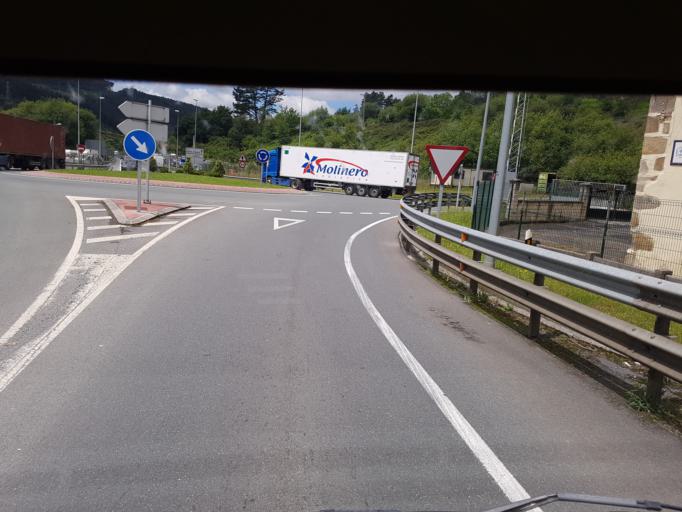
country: ES
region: Basque Country
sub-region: Bizkaia
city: Amorebieta
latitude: 43.2310
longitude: -2.7779
